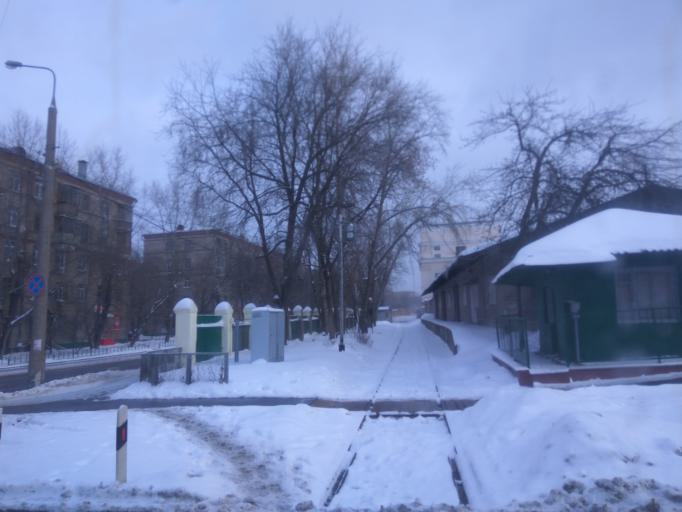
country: RU
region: Moscow
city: Mar'ina Roshcha
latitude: 55.8040
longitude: 37.5740
